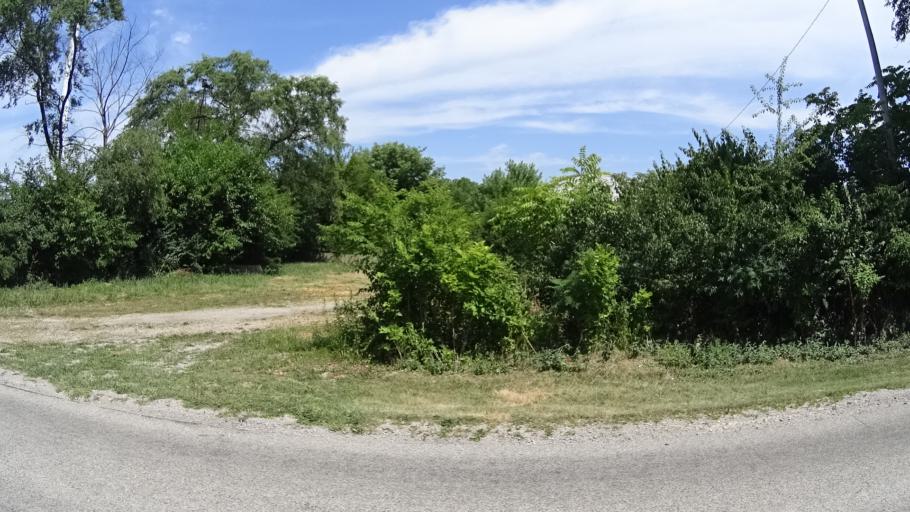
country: US
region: Ohio
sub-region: Erie County
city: Sandusky
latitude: 41.3958
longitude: -82.7879
